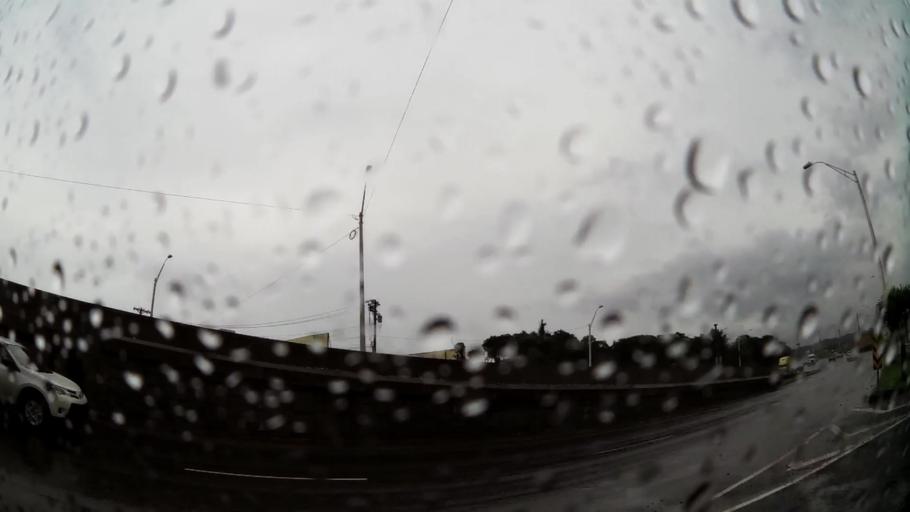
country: PA
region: Colon
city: Arco Iris
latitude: 9.3367
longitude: -79.8872
